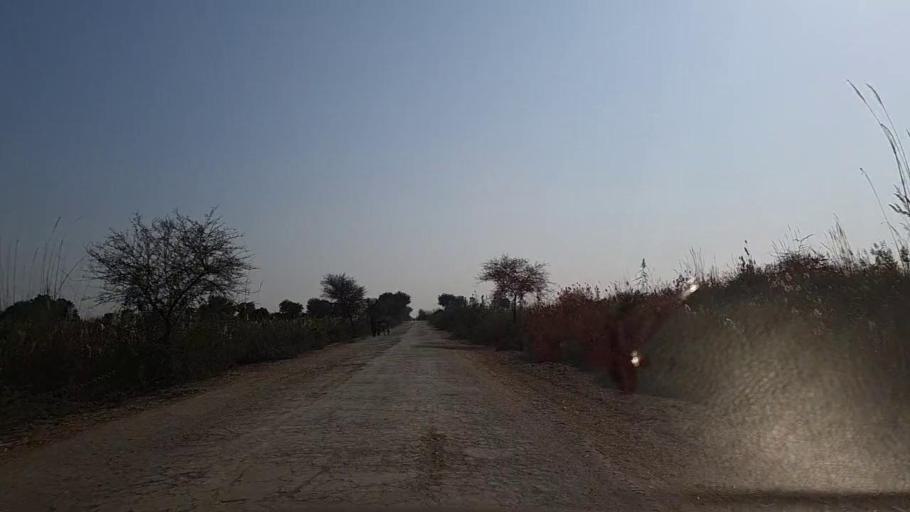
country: PK
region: Sindh
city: Tando Mittha Khan
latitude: 25.9002
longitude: 69.0771
